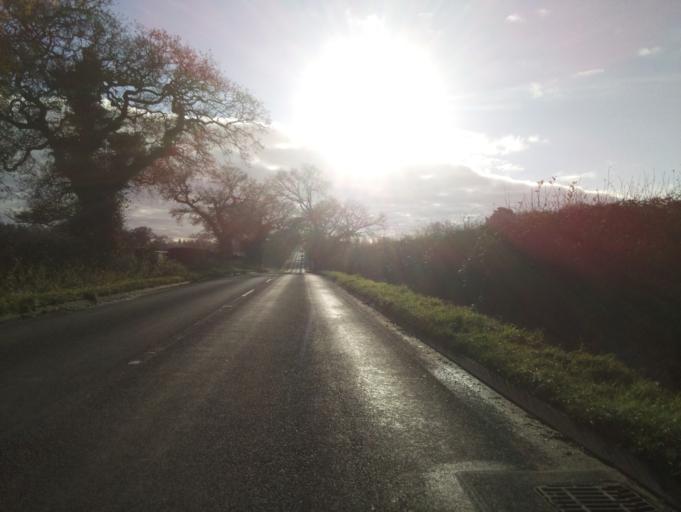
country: GB
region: England
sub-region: Staffordshire
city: Barton under Needwood
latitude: 52.8125
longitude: -1.7361
